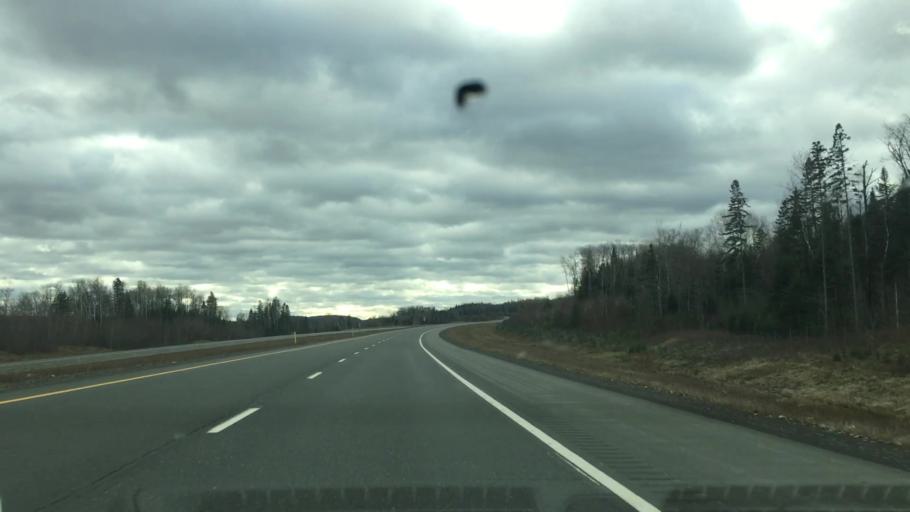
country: US
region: Maine
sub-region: Aroostook County
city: Fort Fairfield
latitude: 46.6749
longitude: -67.7301
